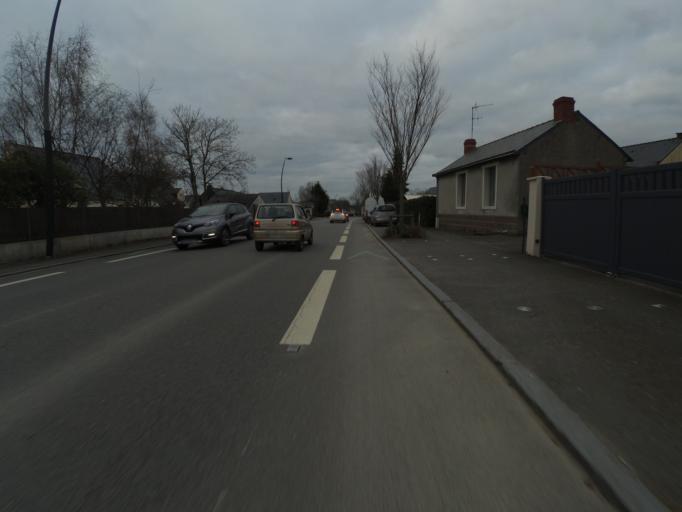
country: FR
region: Pays de la Loire
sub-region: Departement de la Loire-Atlantique
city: Carquefou
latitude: 47.3031
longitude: -1.4860
